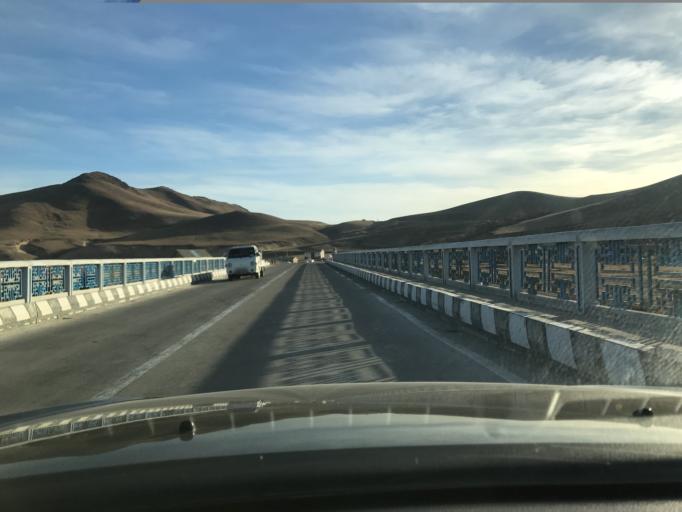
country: MN
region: Central Aimak
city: Dzuunmod
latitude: 47.8215
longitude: 107.3309
